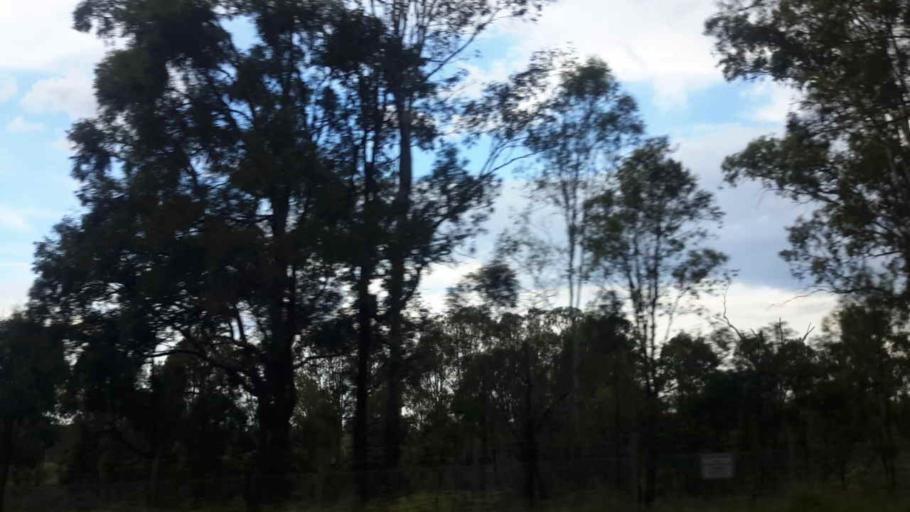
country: AU
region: New South Wales
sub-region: Penrith Municipality
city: Glenmore Park
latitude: -33.8055
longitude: 150.6961
